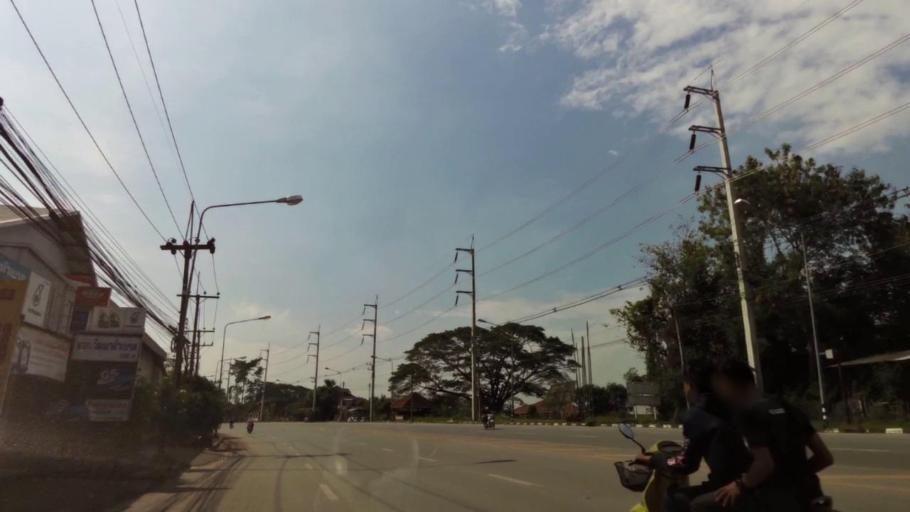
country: TH
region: Chiang Rai
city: Chiang Rai
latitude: 19.8894
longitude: 99.8022
